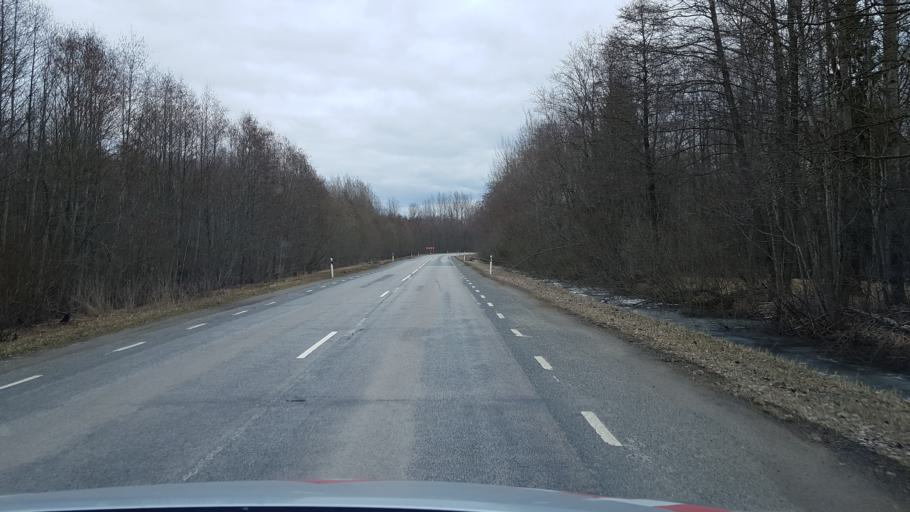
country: EE
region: Ida-Virumaa
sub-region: Narva linn
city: Narva
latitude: 59.3533
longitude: 28.0900
